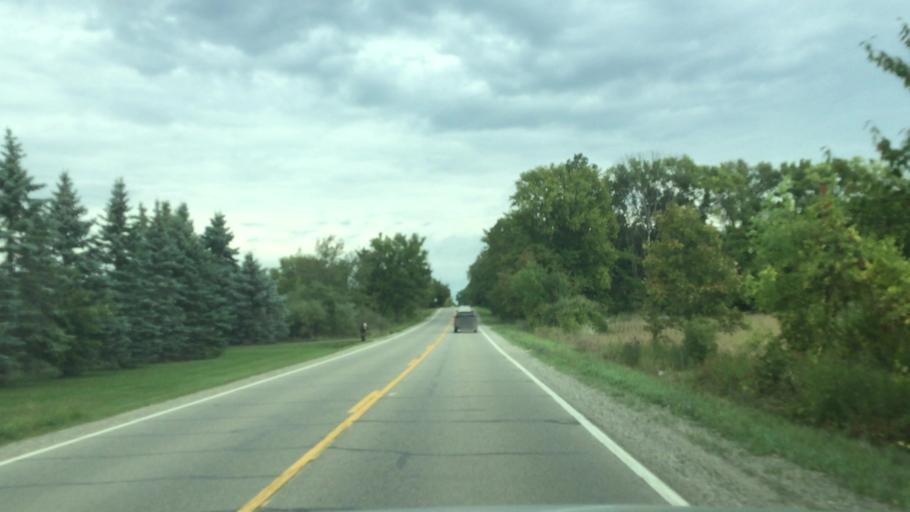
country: US
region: Michigan
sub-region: Livingston County
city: Howell
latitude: 42.6509
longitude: -83.8762
